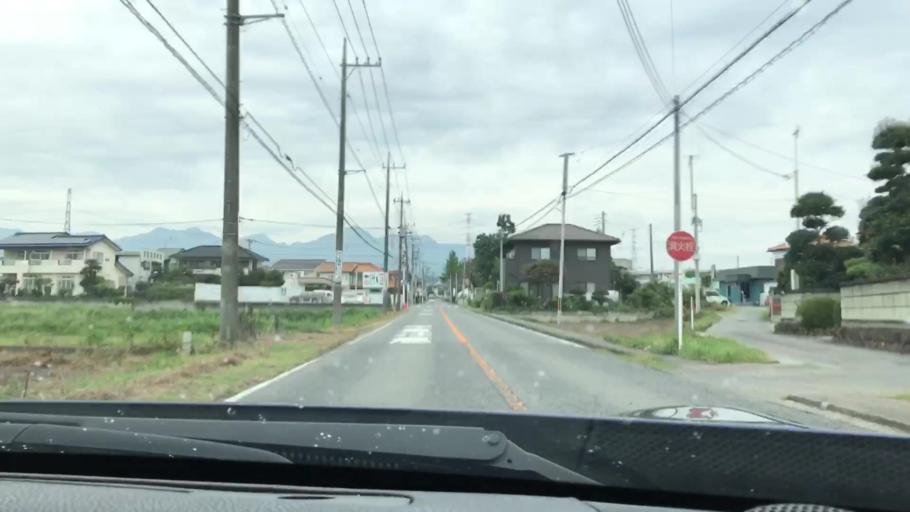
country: JP
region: Gunma
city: Kanekomachi
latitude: 36.3852
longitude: 138.9846
